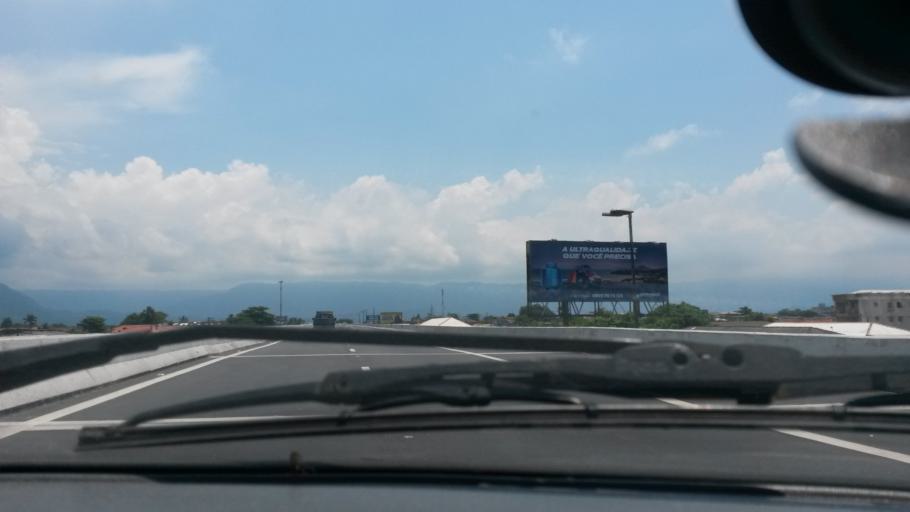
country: BR
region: Sao Paulo
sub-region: Sao Vicente
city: Sao Vicente
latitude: -23.9649
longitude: -46.4012
